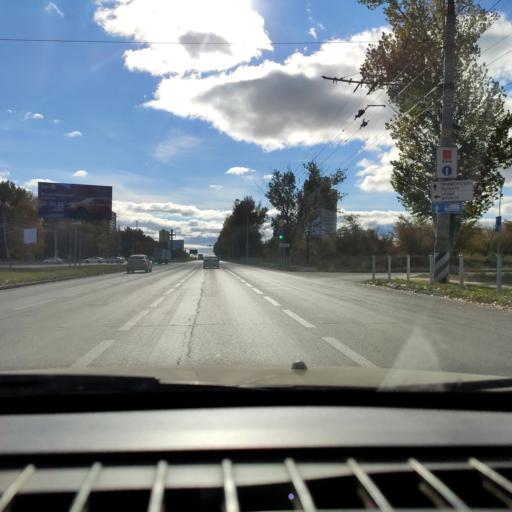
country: RU
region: Samara
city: Tol'yatti
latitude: 53.5179
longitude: 49.2582
